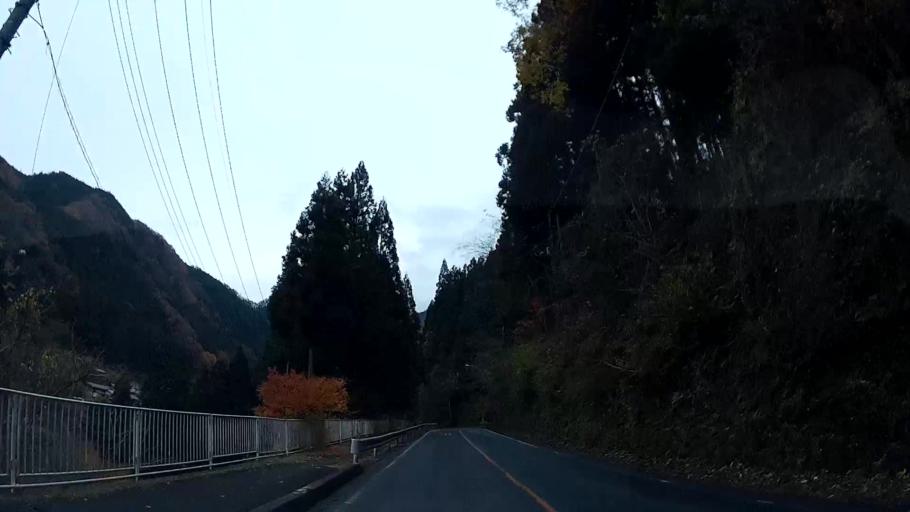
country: JP
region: Saitama
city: Chichibu
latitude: 35.9496
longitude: 138.9643
